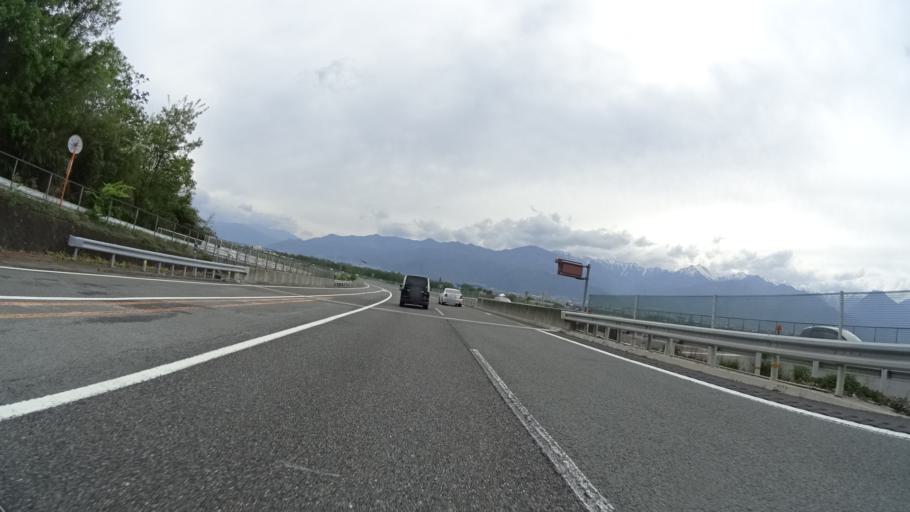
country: JP
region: Nagano
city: Toyoshina
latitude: 36.3278
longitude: 137.9267
